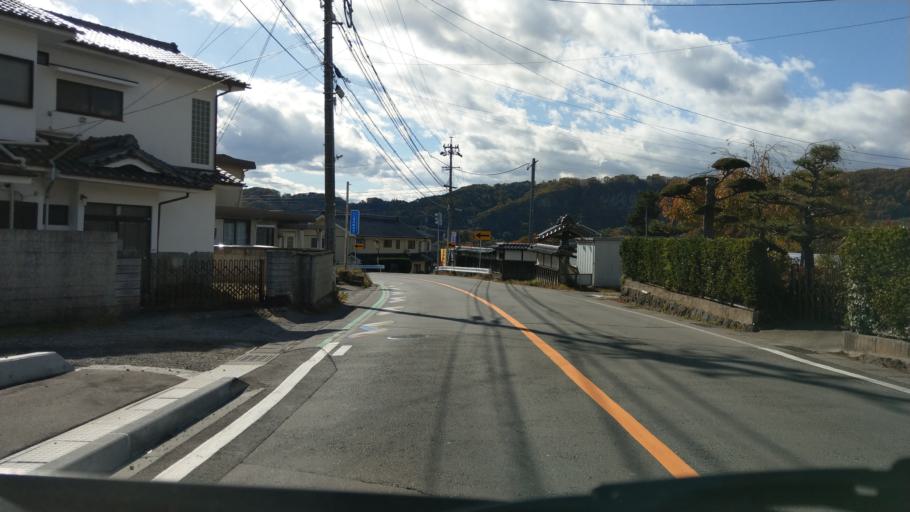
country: JP
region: Nagano
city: Komoro
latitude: 36.3105
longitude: 138.4276
